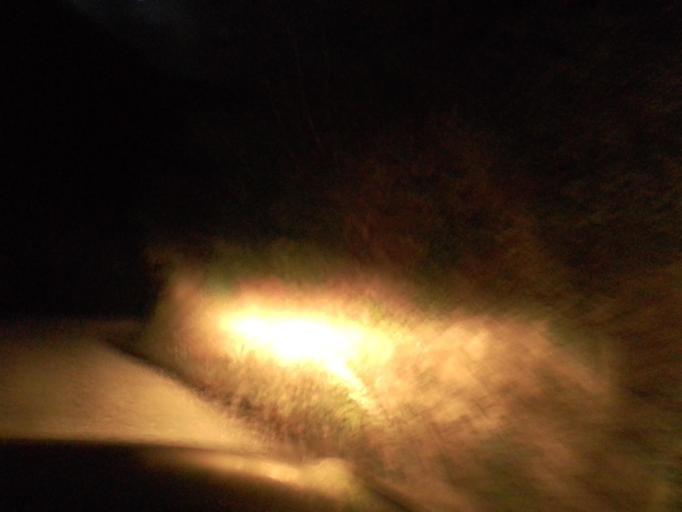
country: MX
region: Chiapas
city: Motozintla de Mendoza
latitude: 15.2401
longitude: -92.2106
